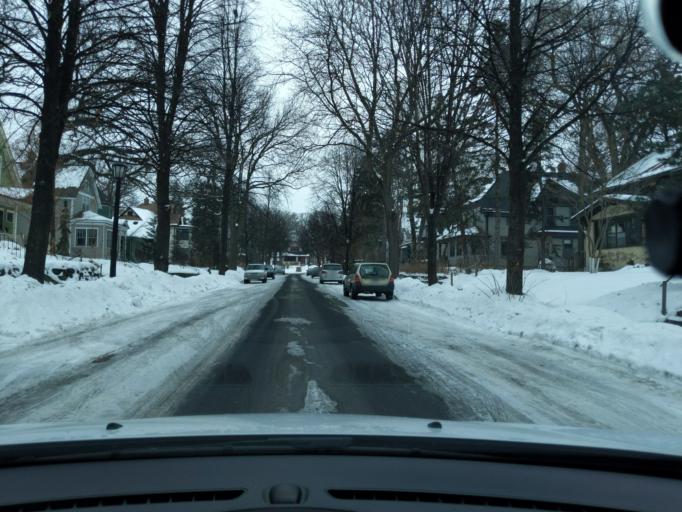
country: US
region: Minnesota
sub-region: Ramsey County
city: Lauderdale
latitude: 44.9633
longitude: -93.2103
